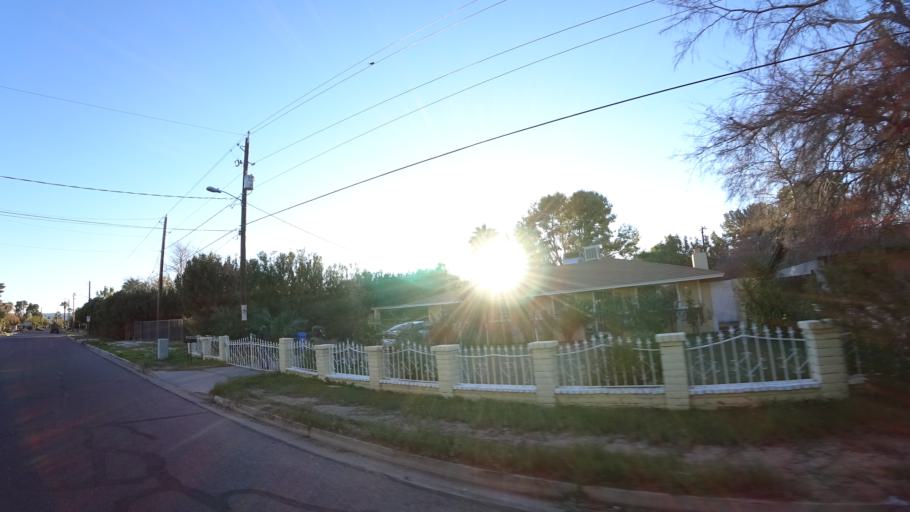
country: US
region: Arizona
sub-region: Maricopa County
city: Phoenix
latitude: 33.4754
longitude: -112.0259
